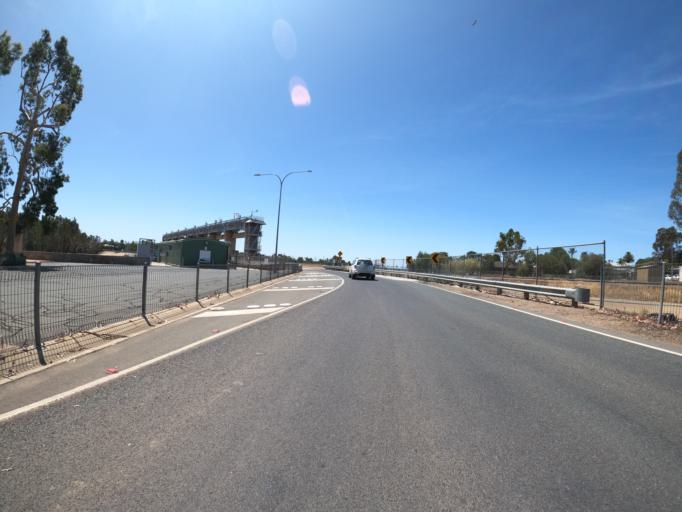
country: AU
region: Victoria
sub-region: Moira
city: Yarrawonga
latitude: -36.0099
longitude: 145.9995
